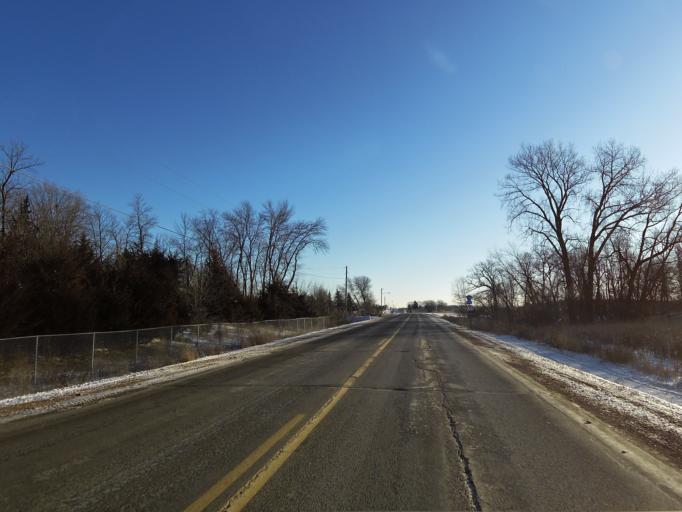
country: US
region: Minnesota
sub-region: Scott County
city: Shakopee
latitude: 44.7322
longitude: -93.5228
